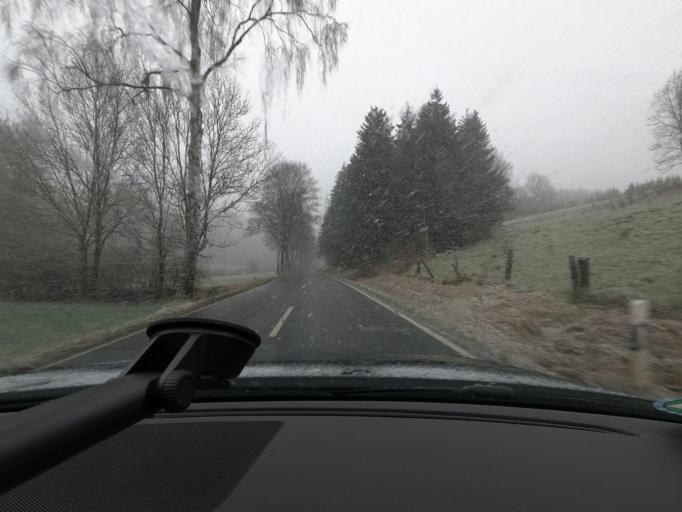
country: DE
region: North Rhine-Westphalia
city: Marsberg
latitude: 51.5066
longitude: 8.8935
